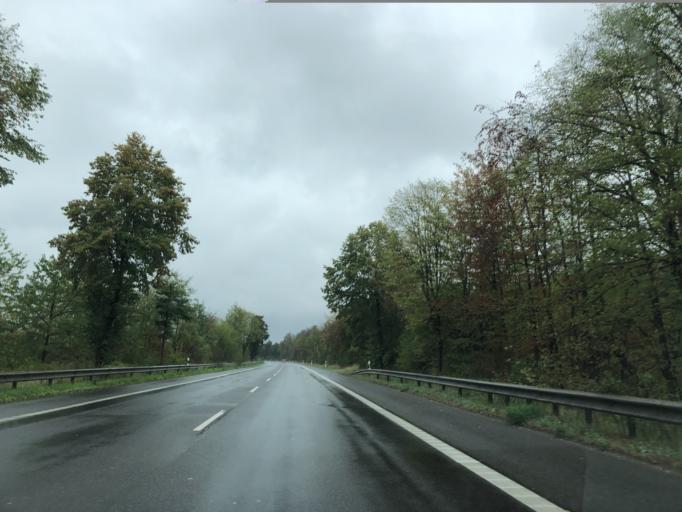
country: DE
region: North Rhine-Westphalia
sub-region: Regierungsbezirk Dusseldorf
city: Grevenbroich
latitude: 51.0719
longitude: 6.5575
